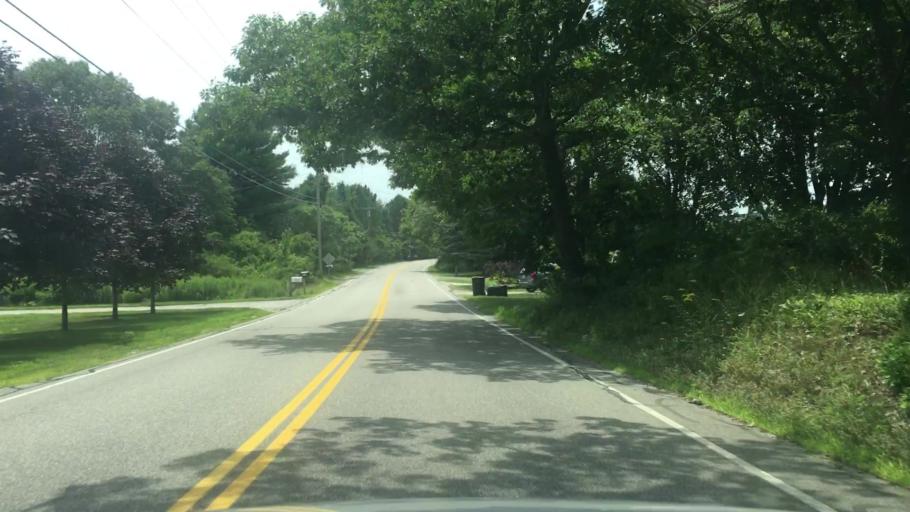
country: US
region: Maine
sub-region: Cumberland County
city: Scarborough
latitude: 43.5799
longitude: -70.2680
